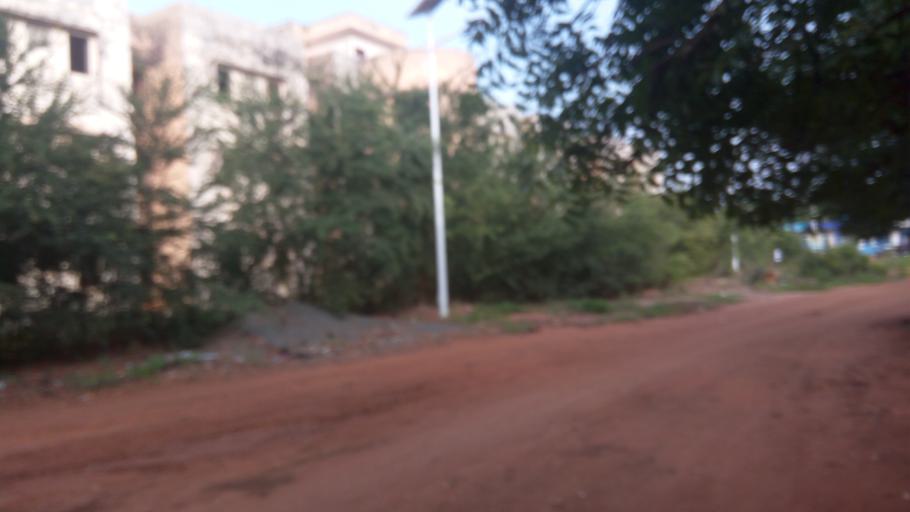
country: TG
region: Maritime
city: Lome
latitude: 6.1687
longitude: 1.2154
